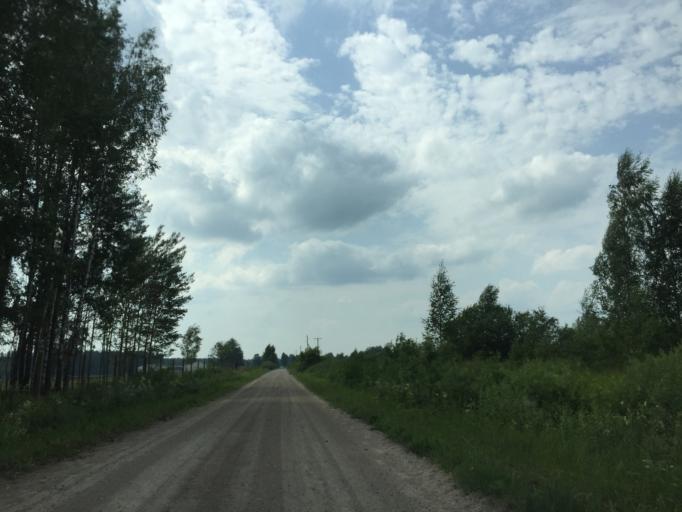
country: LV
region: Ozolnieku
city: Ozolnieki
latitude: 56.7533
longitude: 23.7372
